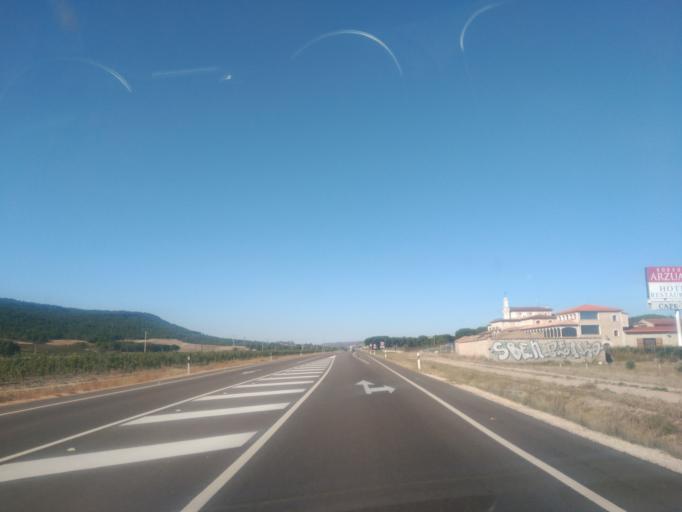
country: ES
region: Castille and Leon
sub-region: Provincia de Valladolid
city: Valbuena de Duero
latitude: 41.6278
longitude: -4.3211
